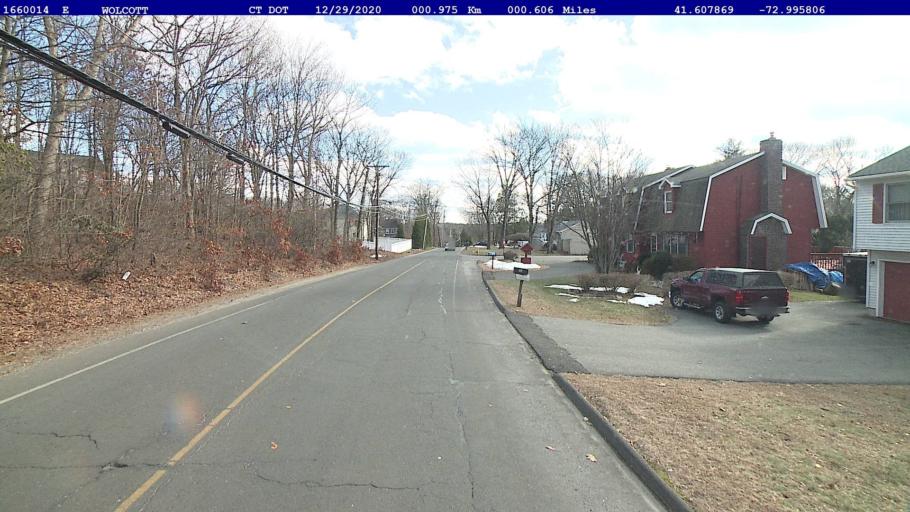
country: US
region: Connecticut
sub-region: New Haven County
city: Wolcott
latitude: 41.6079
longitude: -72.9958
